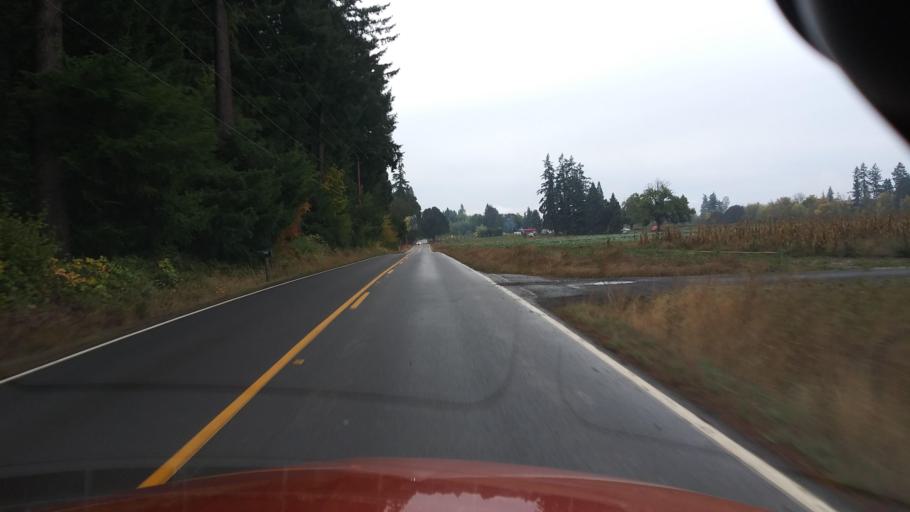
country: US
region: Oregon
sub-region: Washington County
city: Forest Grove
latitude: 45.5369
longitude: -123.0871
